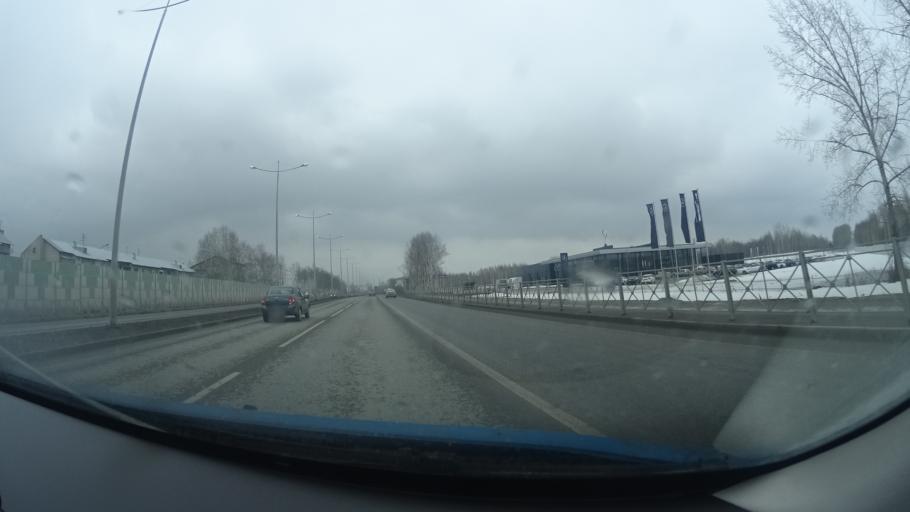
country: RU
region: Perm
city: Kondratovo
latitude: 57.9421
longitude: 56.0643
